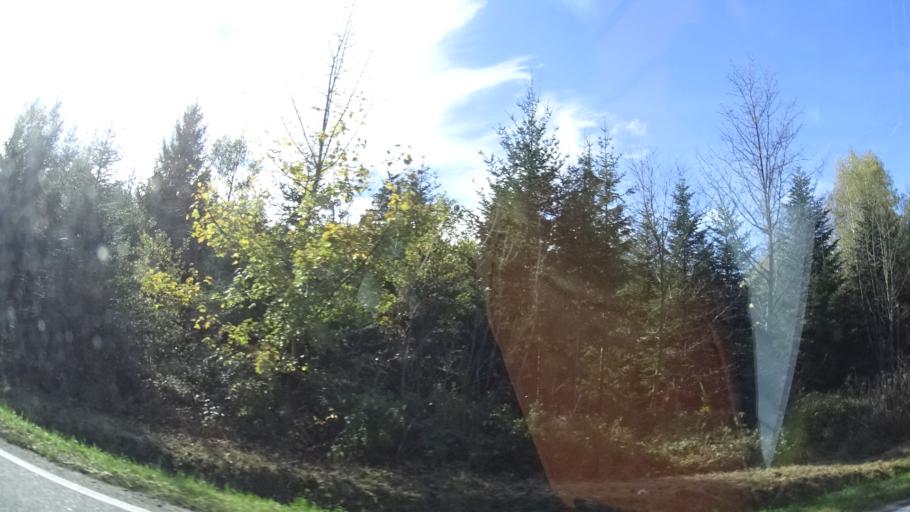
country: DE
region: Baden-Wuerttemberg
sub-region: Karlsruhe Region
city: Unterreichenbach
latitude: 48.8625
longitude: 8.7513
